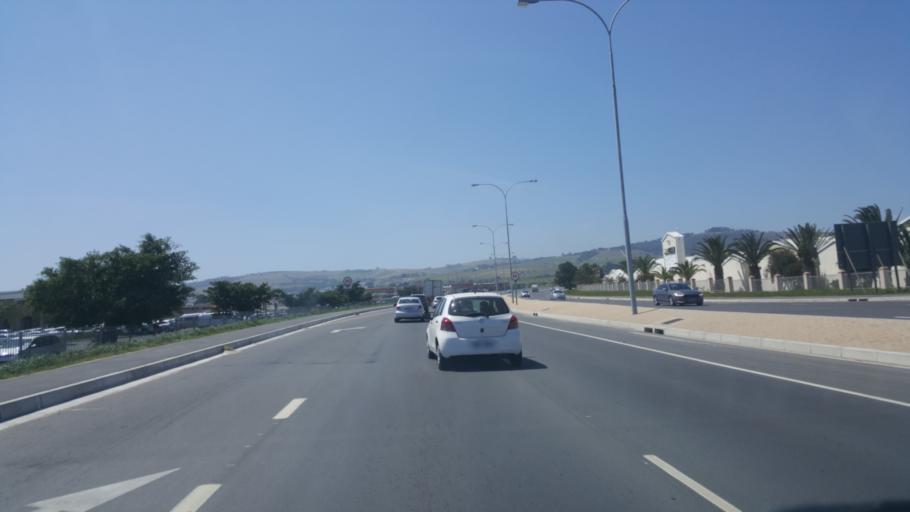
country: ZA
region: Western Cape
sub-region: City of Cape Town
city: Kraaifontein
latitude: -33.9508
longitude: 18.6970
